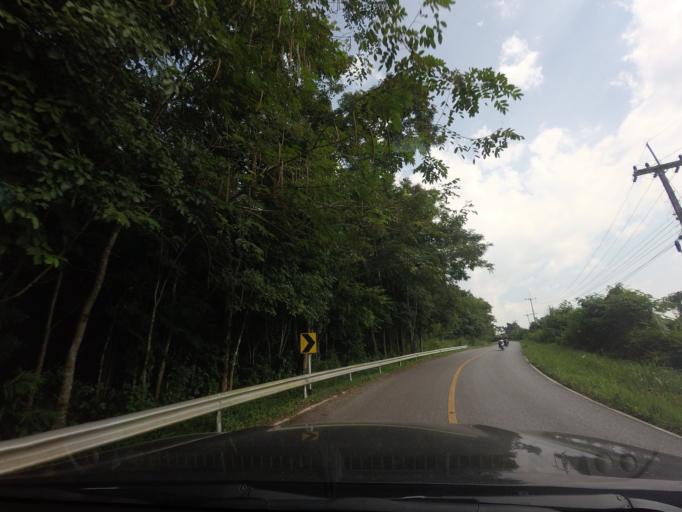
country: TH
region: Phitsanulok
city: Nakhon Thai
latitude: 17.0212
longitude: 100.9438
